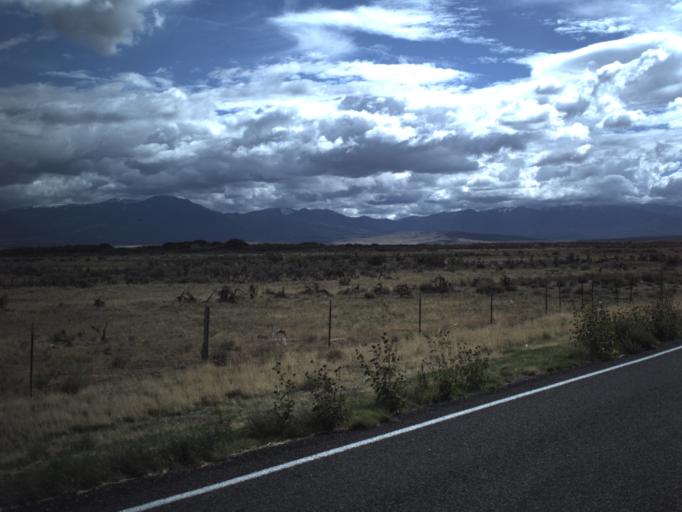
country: US
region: Utah
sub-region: Millard County
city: Fillmore
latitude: 39.1401
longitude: -112.4097
